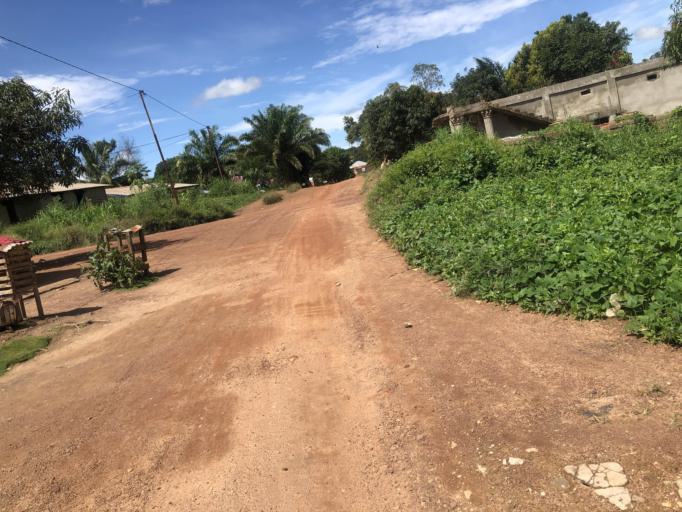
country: SL
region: Eastern Province
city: Koidu
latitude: 8.6402
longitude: -10.9507
